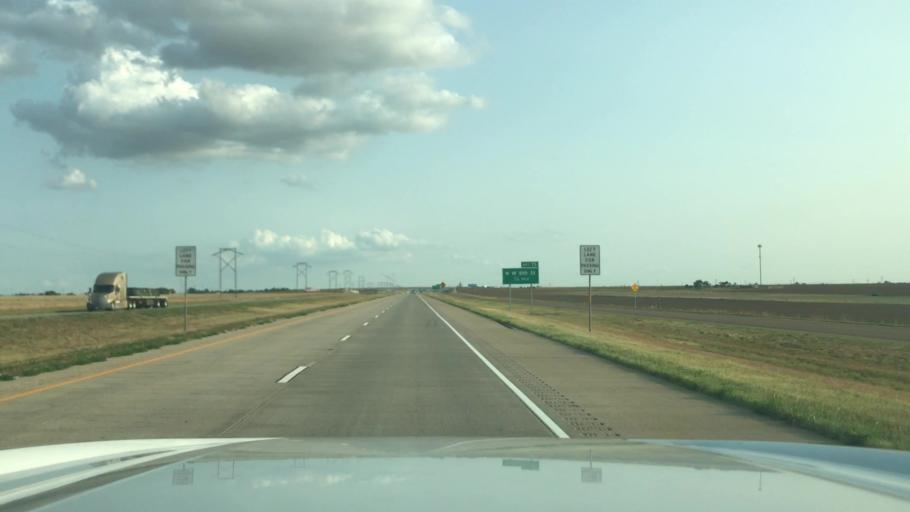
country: US
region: Texas
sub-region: Swisher County
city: Tulia
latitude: 34.5534
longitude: -101.7950
